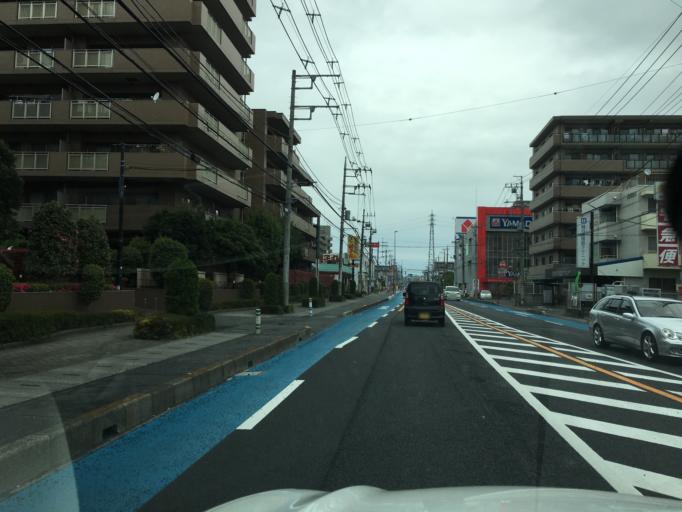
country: JP
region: Saitama
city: Koshigaya
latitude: 35.8776
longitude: 139.7932
